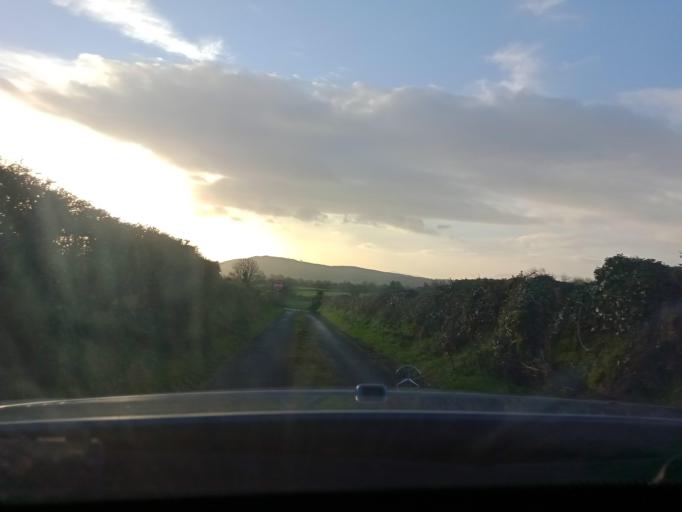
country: IE
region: Leinster
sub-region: Kilkenny
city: Callan
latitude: 52.4613
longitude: -7.4212
